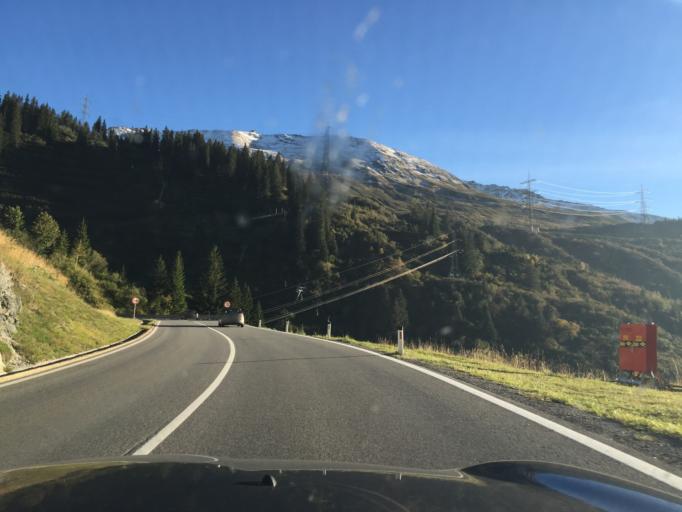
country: AT
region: Vorarlberg
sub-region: Politischer Bezirk Bludenz
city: Lech
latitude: 47.1392
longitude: 10.1621
